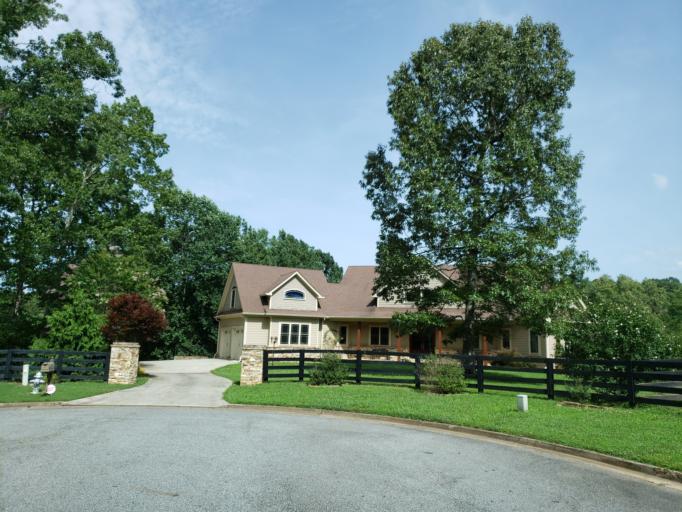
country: US
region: Georgia
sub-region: Cherokee County
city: Ball Ground
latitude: 34.3098
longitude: -84.4411
